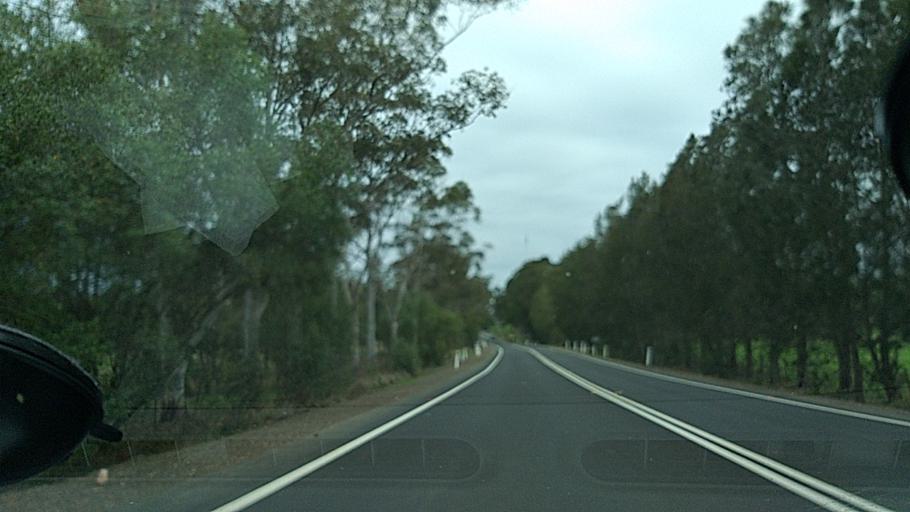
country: AU
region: New South Wales
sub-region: Camden
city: Camden South
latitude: -34.1262
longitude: 150.7009
